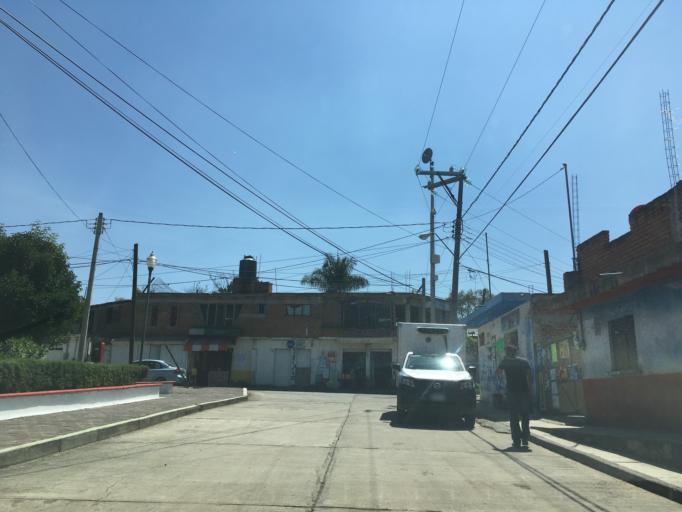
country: MX
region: Michoacan
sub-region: Morelia
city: Morelos
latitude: 19.6502
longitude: -101.2334
